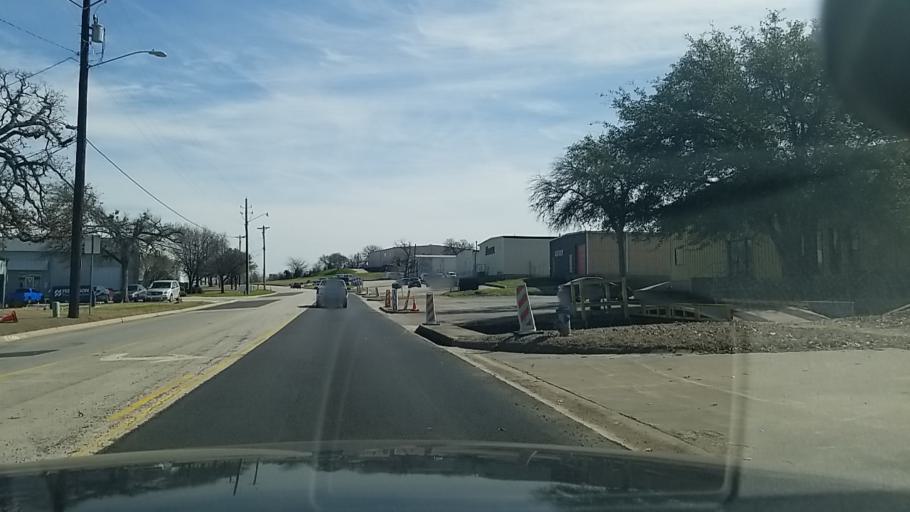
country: US
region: Texas
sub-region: Denton County
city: Denton
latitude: 33.2002
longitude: -97.1197
